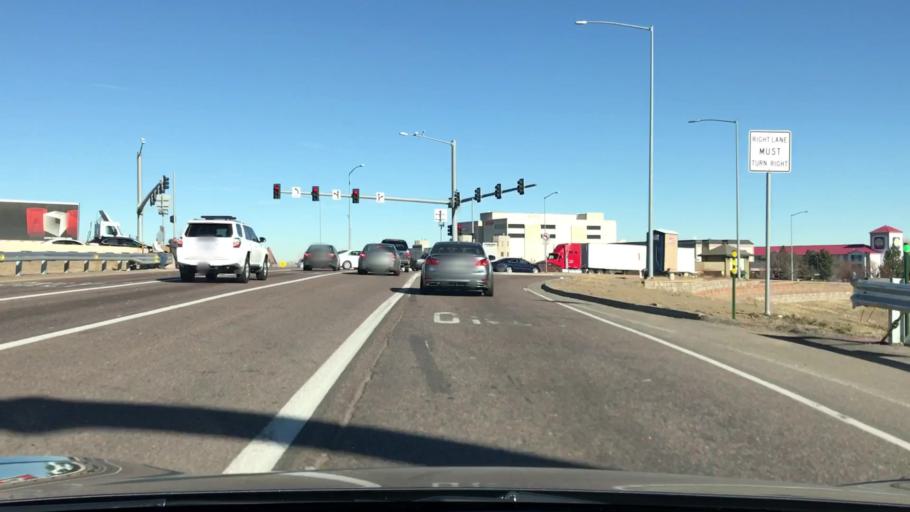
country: US
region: Colorado
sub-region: Adams County
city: Northglenn
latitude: 39.9135
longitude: -104.9892
